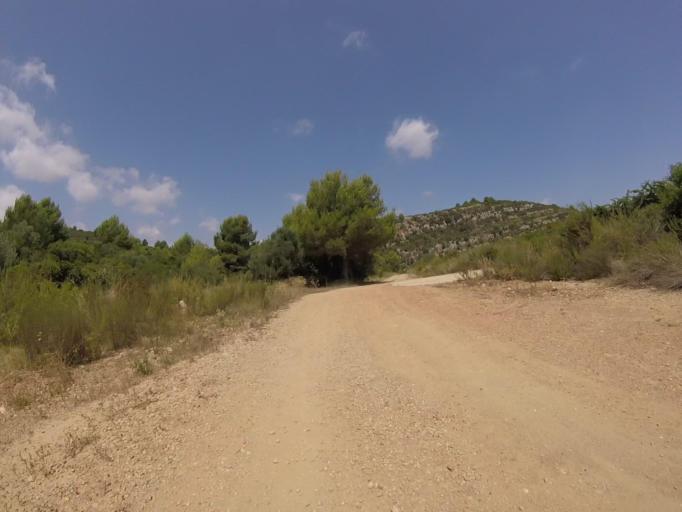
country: ES
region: Valencia
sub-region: Provincia de Castello
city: Torreblanca
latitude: 40.2200
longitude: 0.1483
